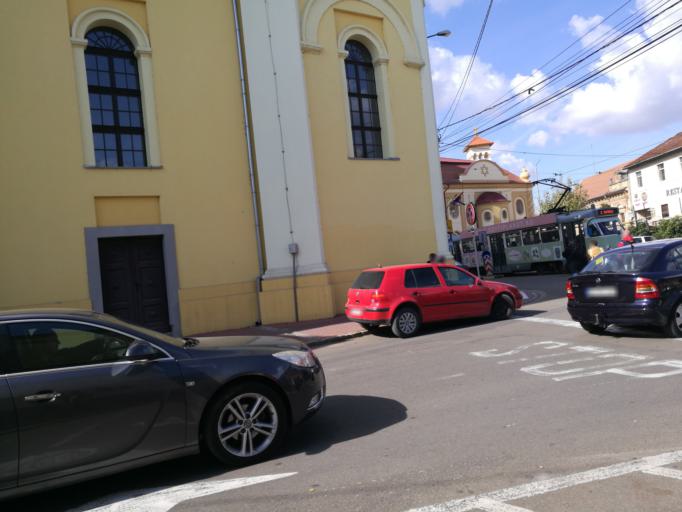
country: RO
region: Bihor
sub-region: Comuna Biharea
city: Oradea
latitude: 47.0565
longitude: 21.9237
